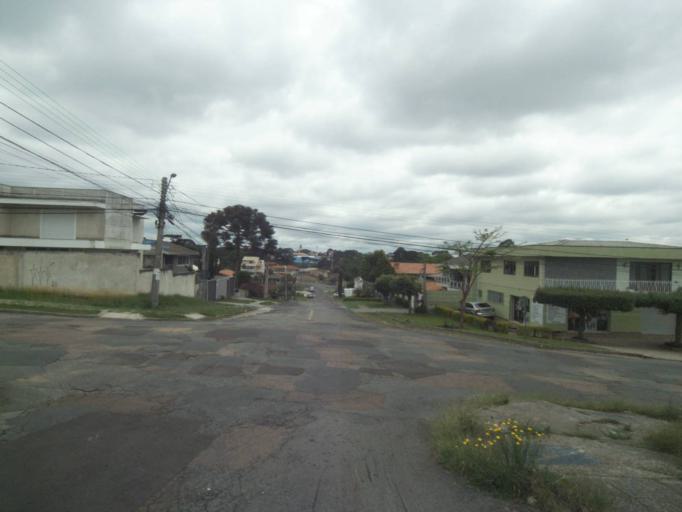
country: BR
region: Parana
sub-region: Curitiba
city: Curitiba
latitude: -25.3883
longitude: -49.2774
